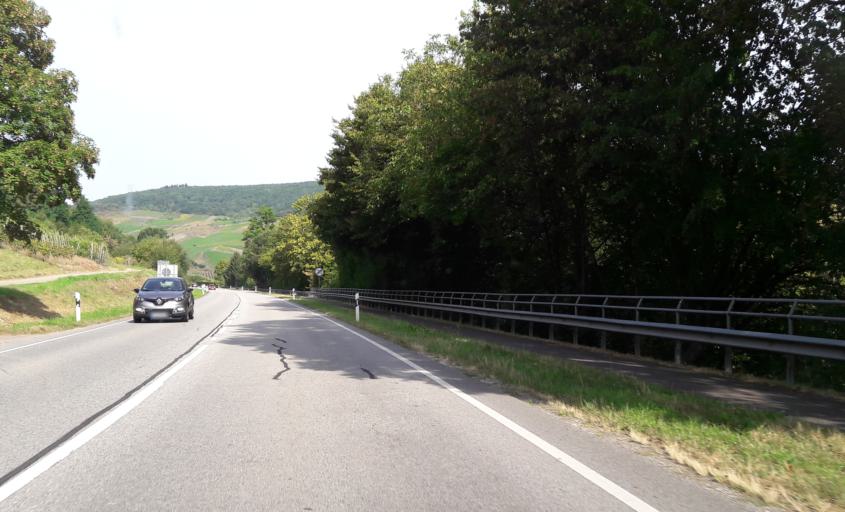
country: DE
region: Rheinland-Pfalz
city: Zell
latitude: 50.0326
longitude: 7.1728
